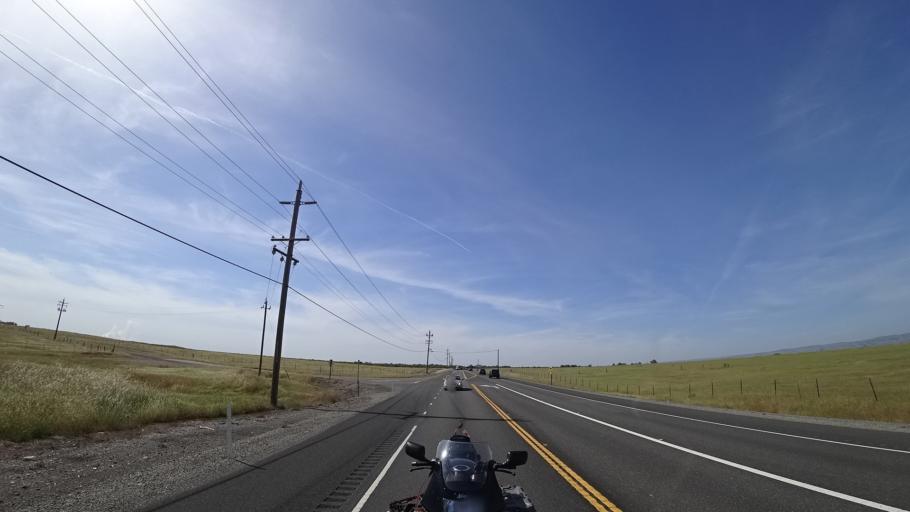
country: US
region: California
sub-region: Glenn County
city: Hamilton City
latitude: 39.8633
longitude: -121.9599
